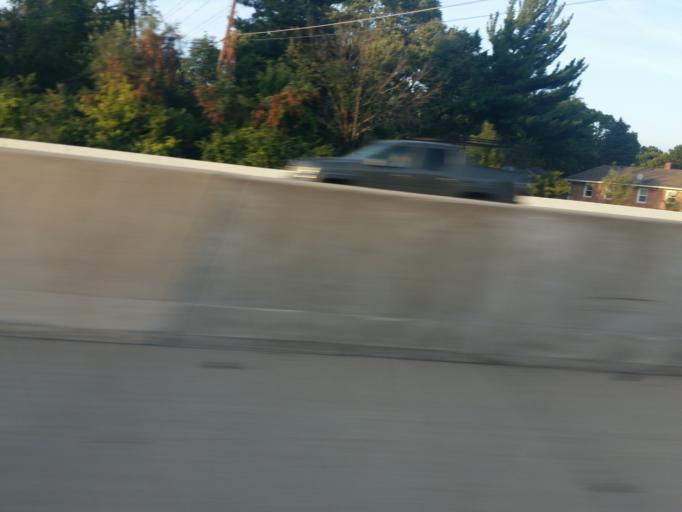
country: US
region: Indiana
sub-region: Marion County
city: Meridian Hills
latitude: 39.9232
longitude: -86.1184
